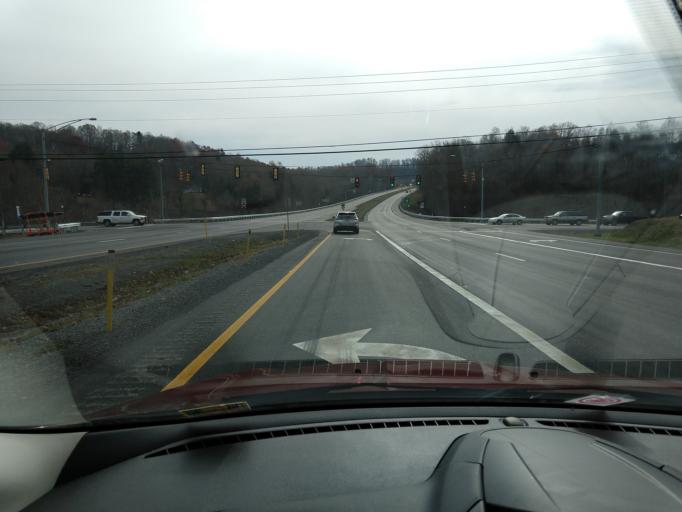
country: US
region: West Virginia
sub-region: Nicholas County
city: Summersville
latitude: 38.2770
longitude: -80.8361
